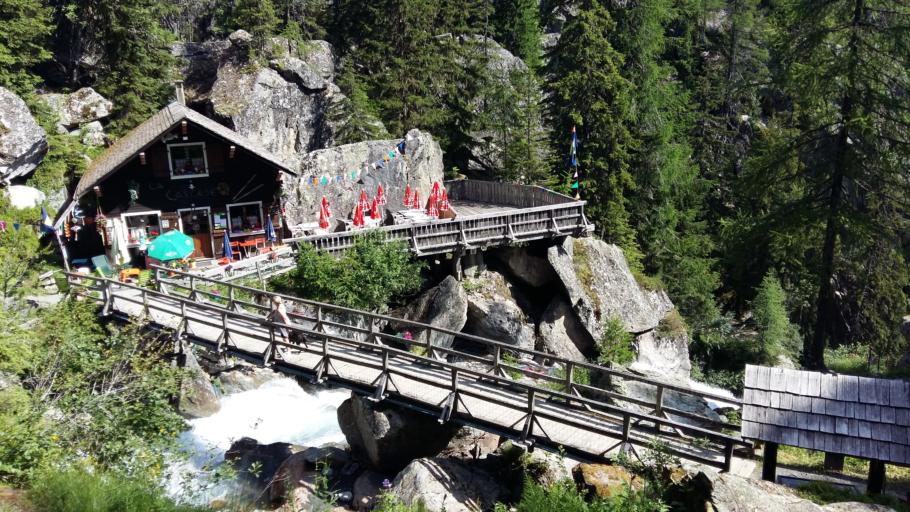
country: FR
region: Rhone-Alpes
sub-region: Departement de la Haute-Savoie
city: Chamonix-Mont-Blanc
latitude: 46.0198
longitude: 6.9116
